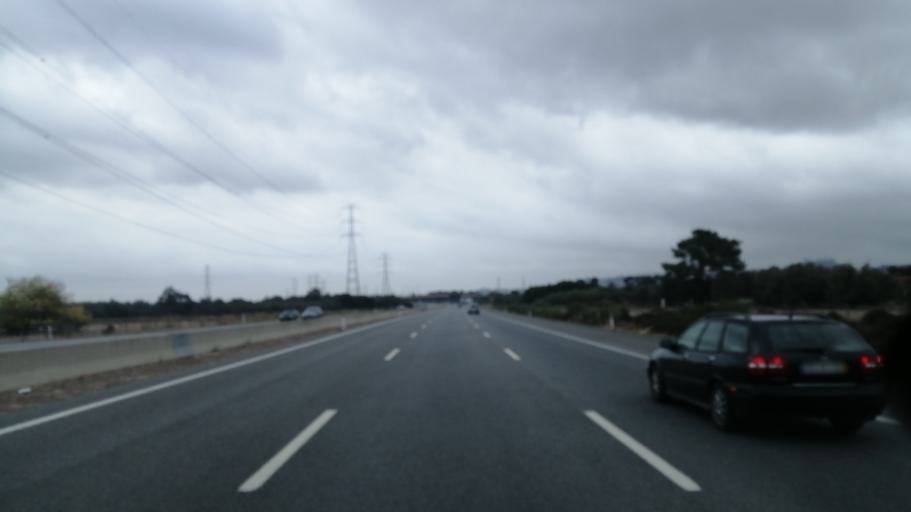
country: PT
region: Setubal
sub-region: Palmela
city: Quinta do Anjo
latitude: 38.5838
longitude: -8.9467
